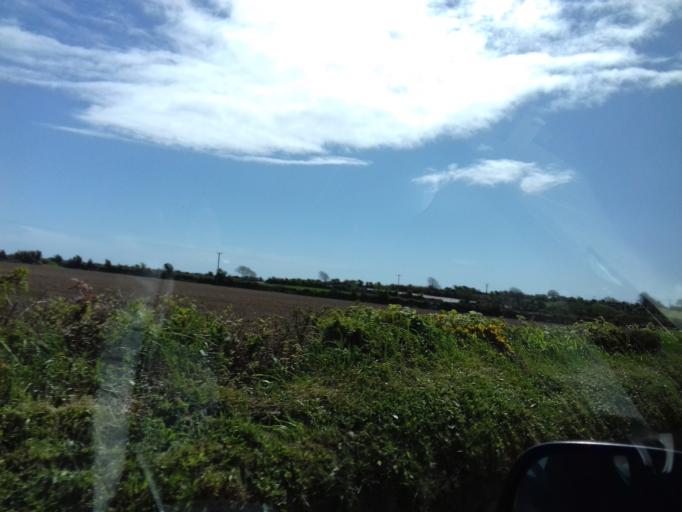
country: IE
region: Munster
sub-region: Waterford
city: Dunmore East
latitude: 52.2289
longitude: -6.8625
